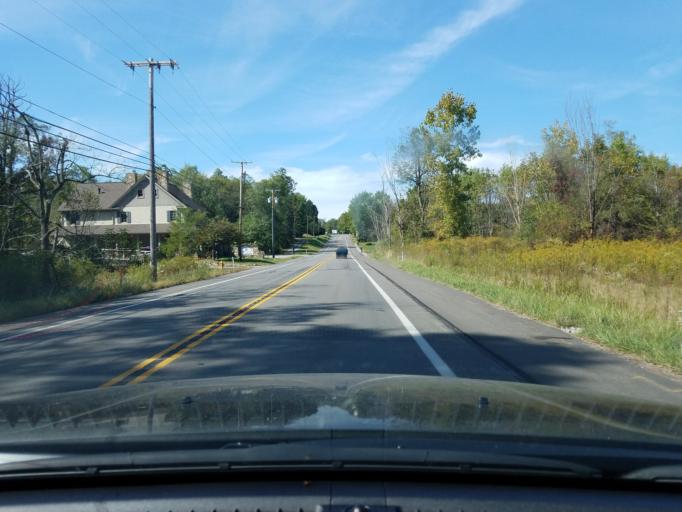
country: US
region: Pennsylvania
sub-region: Lawrence County
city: New Castle
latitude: 40.9570
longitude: -80.2872
